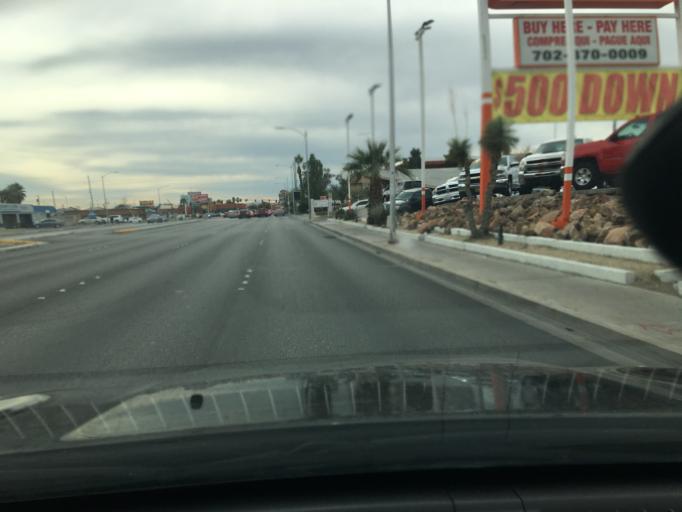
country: US
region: Nevada
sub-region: Clark County
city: Spring Valley
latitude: 36.1616
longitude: -115.2062
